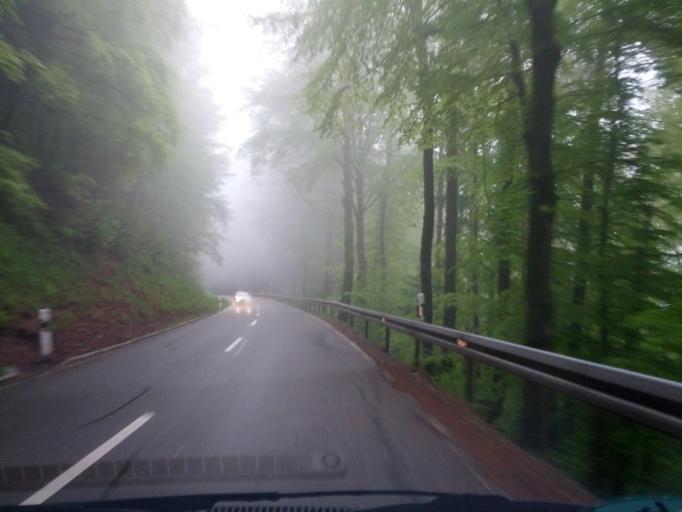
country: DE
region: Baden-Wuerttemberg
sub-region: Freiburg Region
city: Wehr
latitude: 47.6221
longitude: 7.9273
